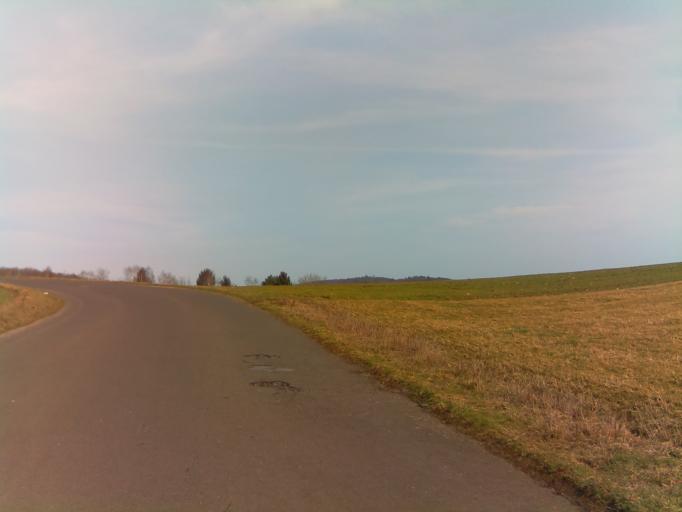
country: DE
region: Rheinland-Pfalz
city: Ellweiler
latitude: 49.6067
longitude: 7.1465
